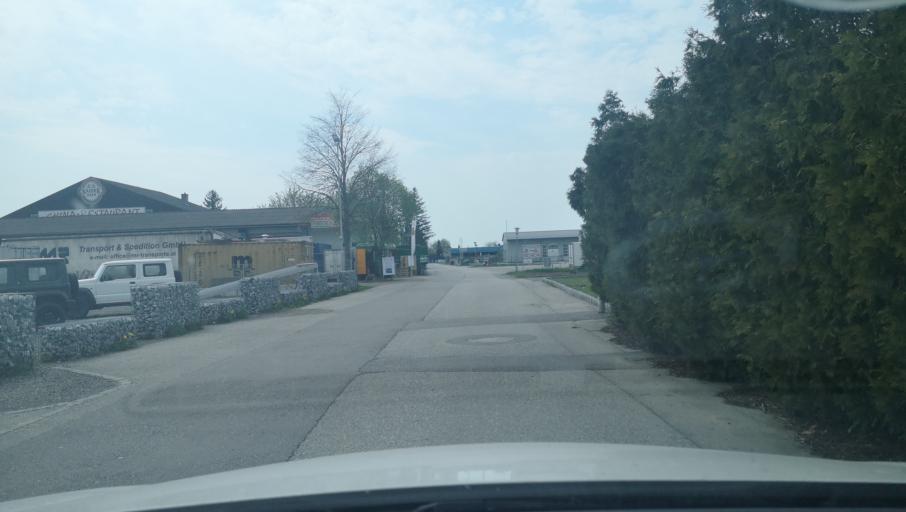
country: AT
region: Lower Austria
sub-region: Politischer Bezirk Amstetten
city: Sankt Georgen am Ybbsfelde
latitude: 48.1148
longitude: 14.9361
